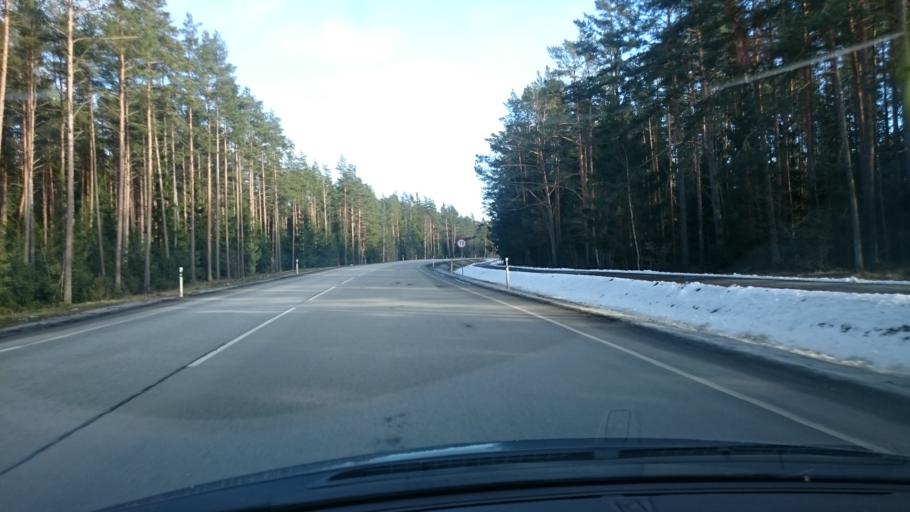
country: EE
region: Harju
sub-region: Kiili vald
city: Kiili
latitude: 59.3537
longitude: 24.7821
